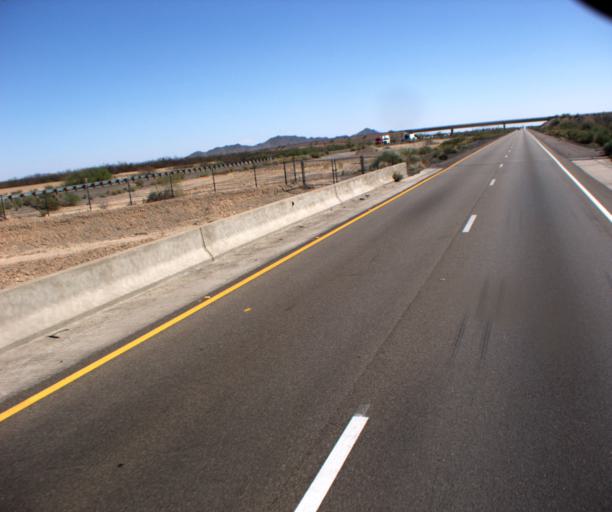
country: US
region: Arizona
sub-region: La Paz County
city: Salome
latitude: 33.5956
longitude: -113.5313
